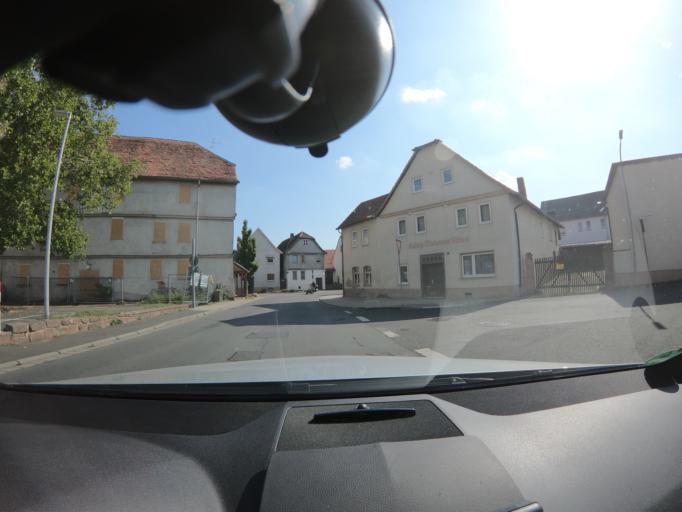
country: DE
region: Hesse
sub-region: Regierungsbezirk Giessen
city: Kirchhain
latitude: 50.8204
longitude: 8.9208
